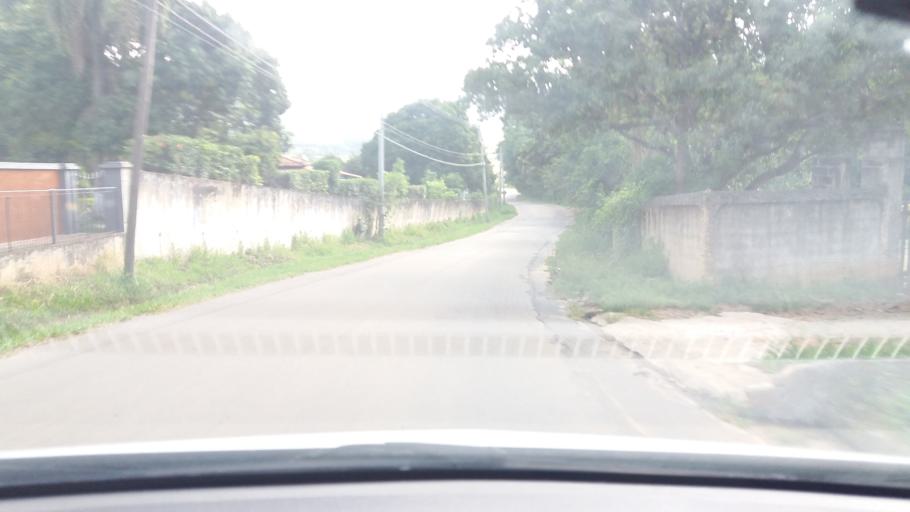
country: BR
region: Sao Paulo
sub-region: Bom Jesus Dos Perdoes
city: Bom Jesus dos Perdoes
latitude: -23.1500
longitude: -46.4701
